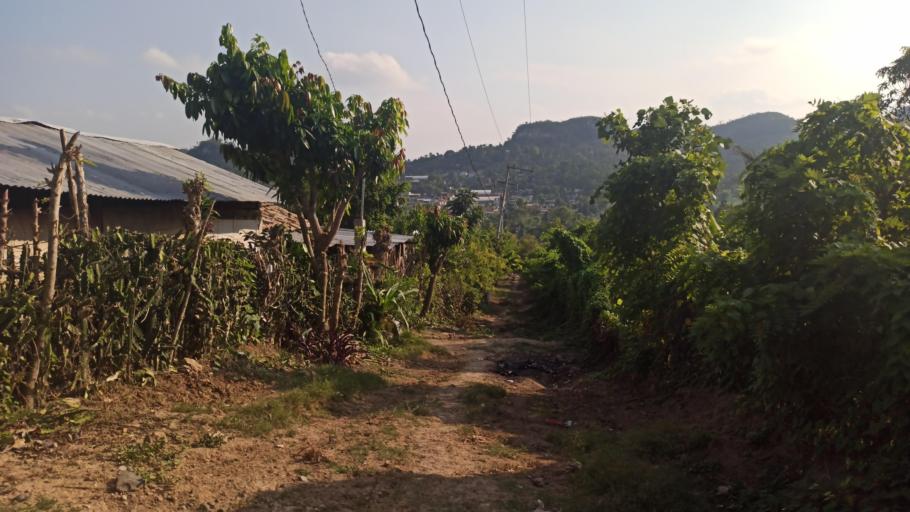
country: MX
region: Veracruz
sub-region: Papantla
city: Polutla
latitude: 20.6024
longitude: -97.2586
